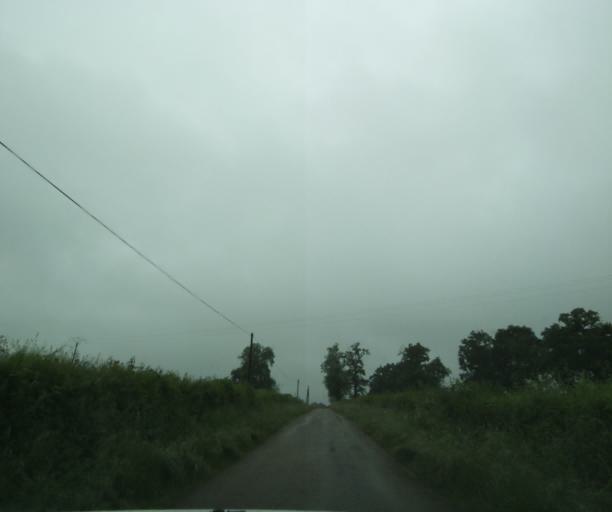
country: FR
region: Bourgogne
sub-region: Departement de Saone-et-Loire
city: Charolles
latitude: 46.3993
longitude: 4.2900
